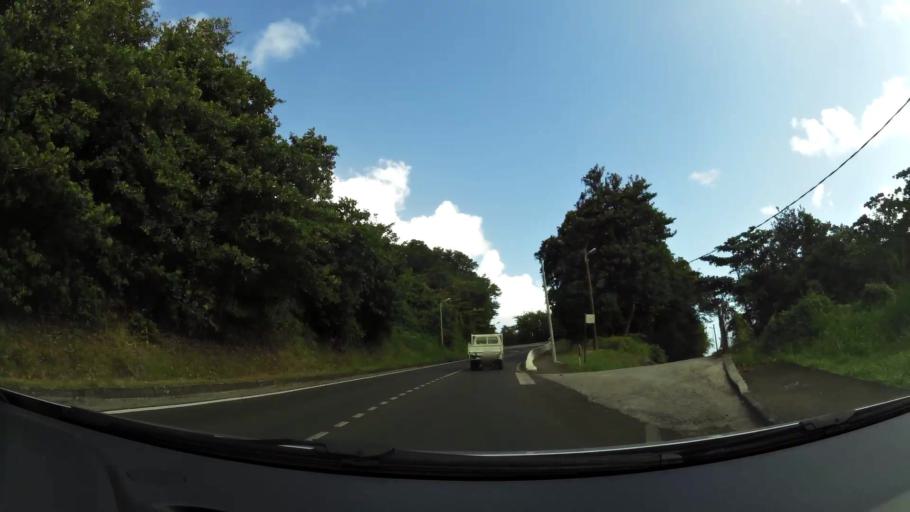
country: MQ
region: Martinique
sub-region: Martinique
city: Le Lorrain
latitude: 14.8256
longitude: -61.0318
